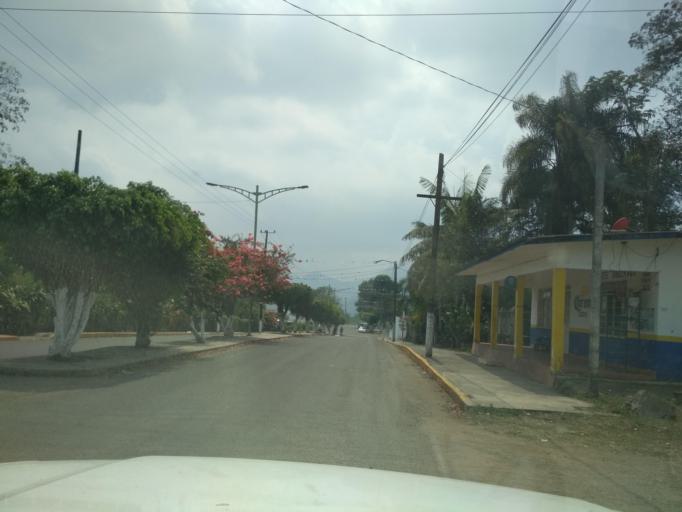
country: MX
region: Veracruz
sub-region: Cordoba
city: San Jose de Tapia
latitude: 18.8512
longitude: -96.9815
